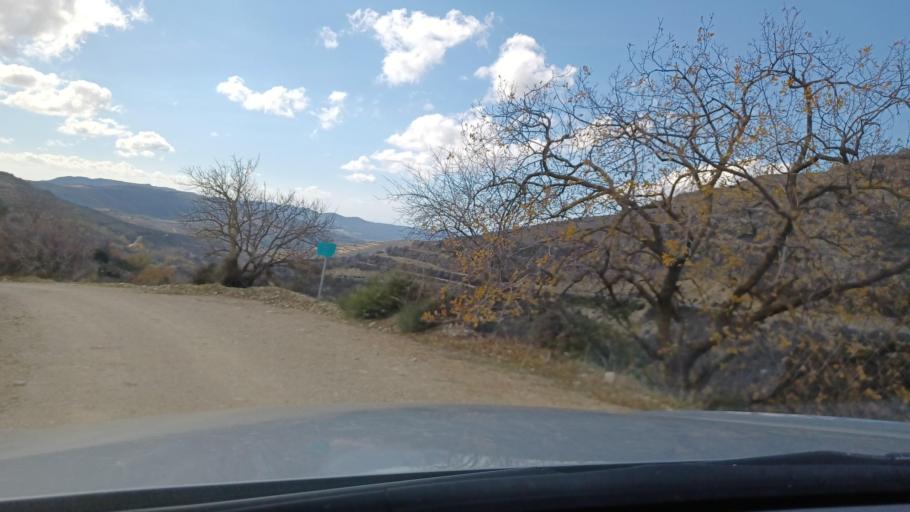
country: CY
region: Limassol
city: Pachna
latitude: 34.8370
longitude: 32.7642
